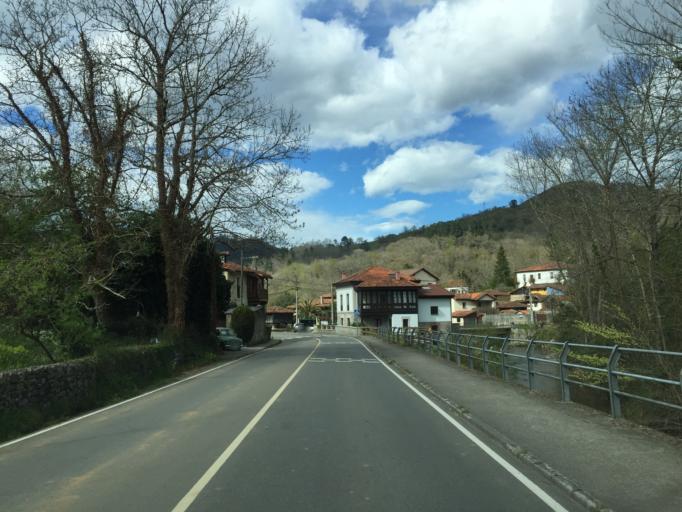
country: ES
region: Asturias
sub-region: Province of Asturias
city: Cangas de Onis
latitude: 43.3433
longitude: -5.0838
